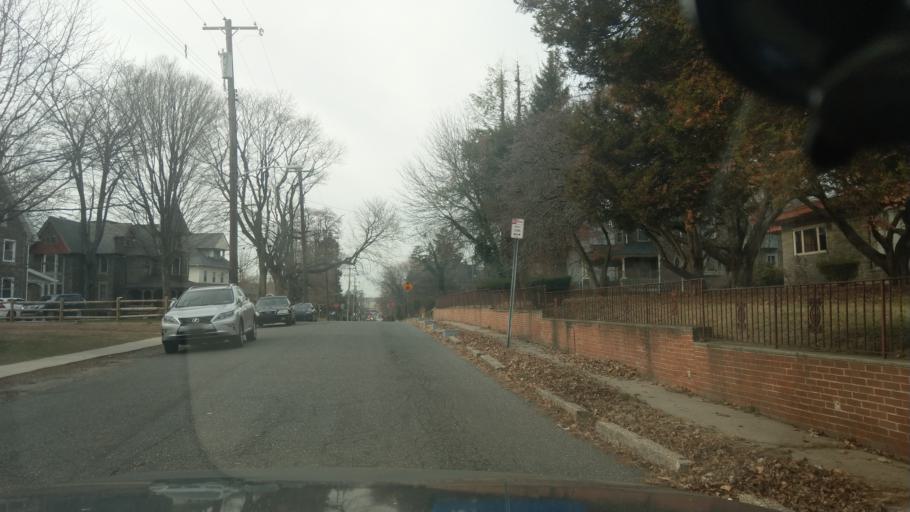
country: US
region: Pennsylvania
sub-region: Montgomery County
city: Jenkintown
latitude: 40.0552
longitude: -75.1334
